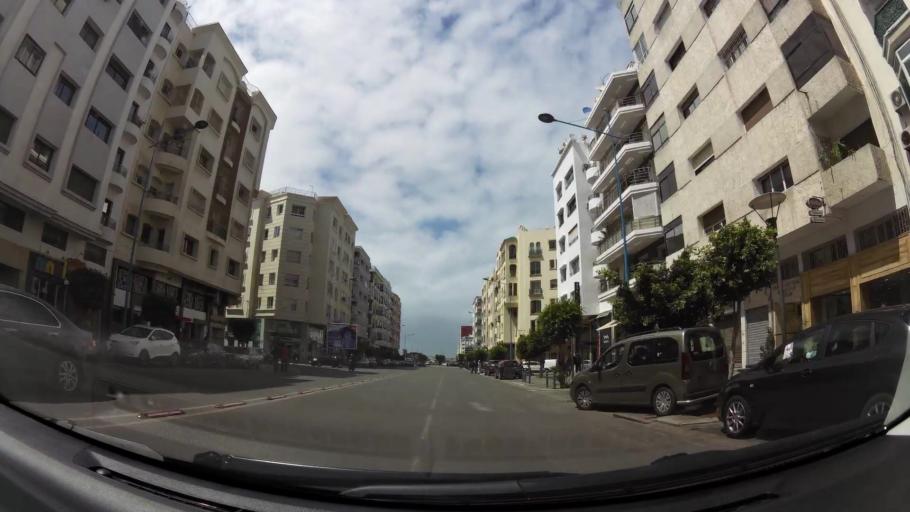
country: MA
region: Grand Casablanca
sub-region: Casablanca
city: Casablanca
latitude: 33.5930
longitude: -7.6432
